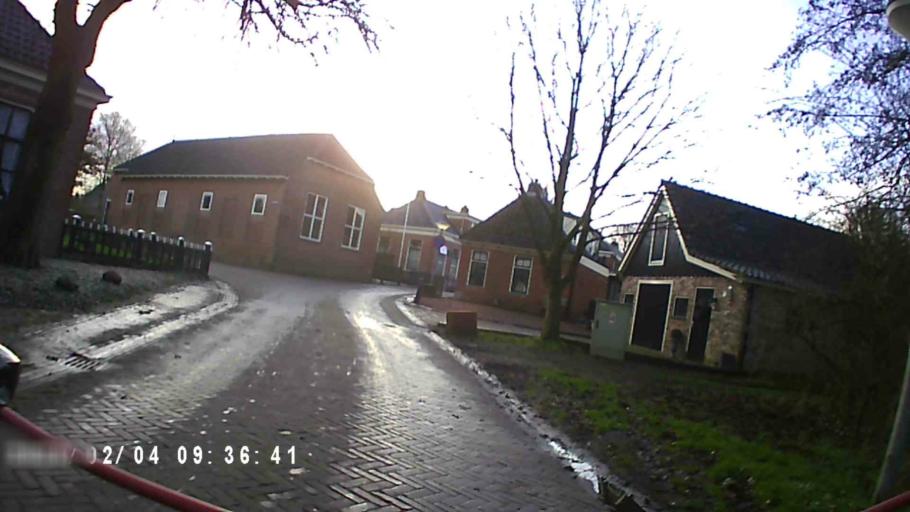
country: NL
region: Groningen
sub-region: Gemeente Zuidhorn
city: Aduard
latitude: 53.3072
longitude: 6.4647
